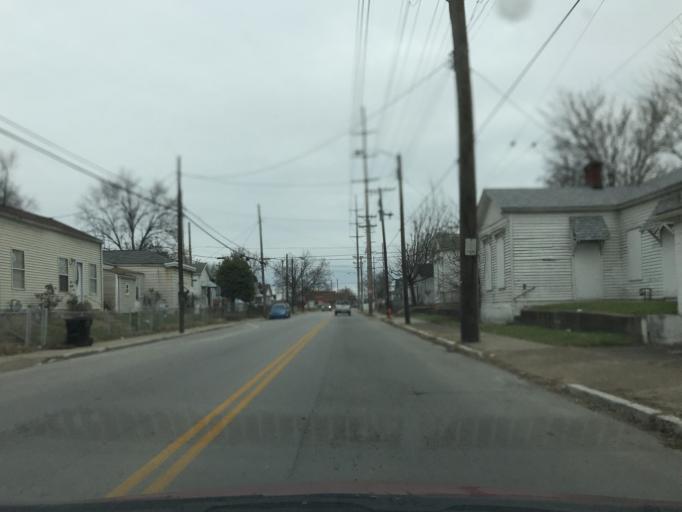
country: US
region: Kentucky
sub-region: Jefferson County
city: Louisville
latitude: 38.2644
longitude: -85.7850
